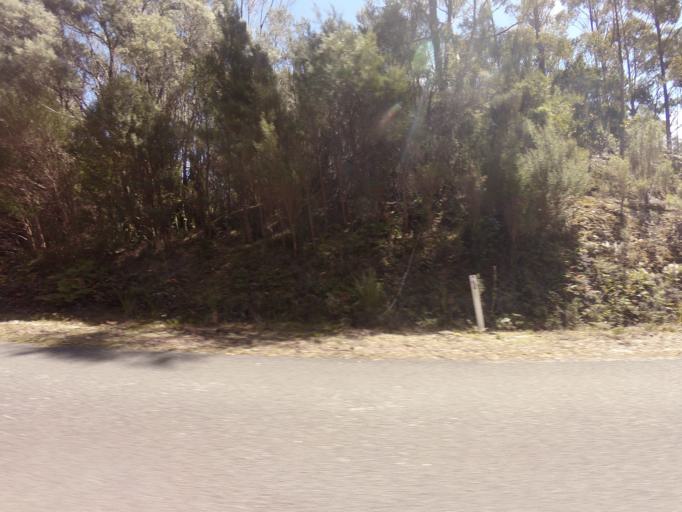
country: AU
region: Tasmania
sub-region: West Coast
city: Queenstown
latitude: -42.7544
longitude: 145.9954
